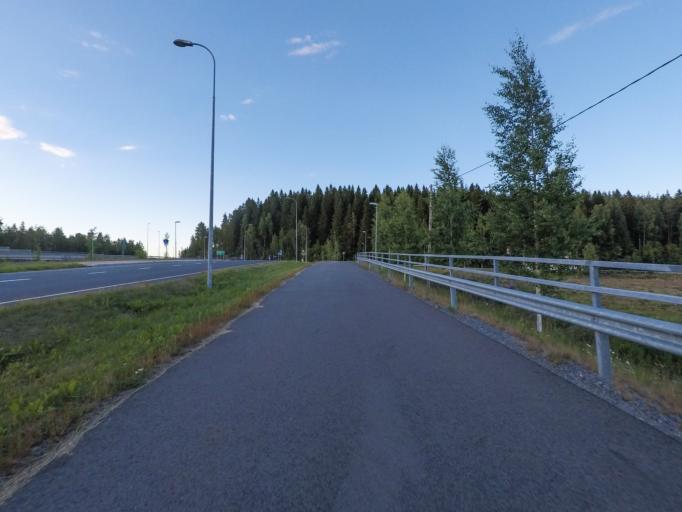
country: FI
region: Northern Savo
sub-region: Kuopio
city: Kuopio
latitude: 62.9570
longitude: 27.6920
